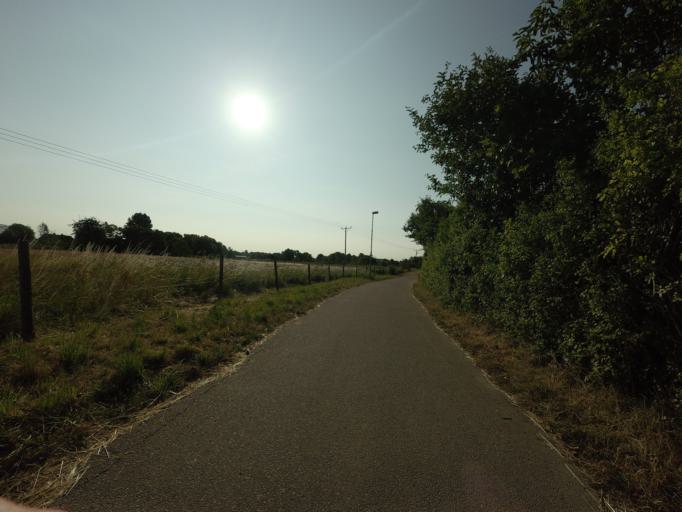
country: SE
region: Skane
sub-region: Landskrona
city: Asmundtorp
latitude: 55.8596
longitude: 12.8954
